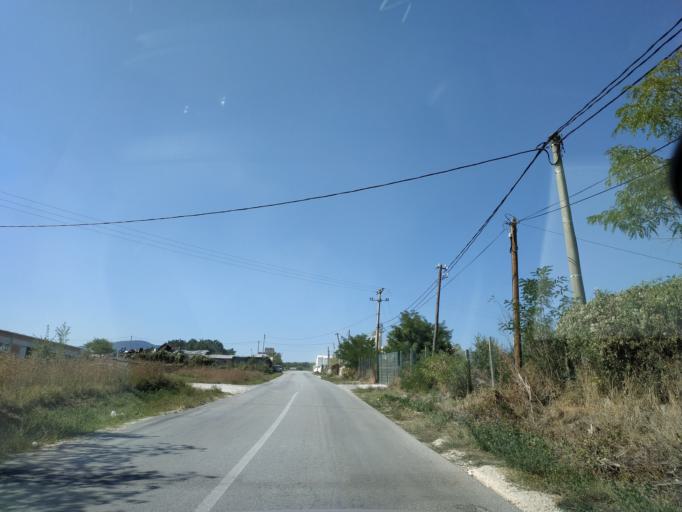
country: RS
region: Central Serbia
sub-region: Sumadijski Okrug
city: Arangelovac
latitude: 44.2960
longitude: 20.5933
